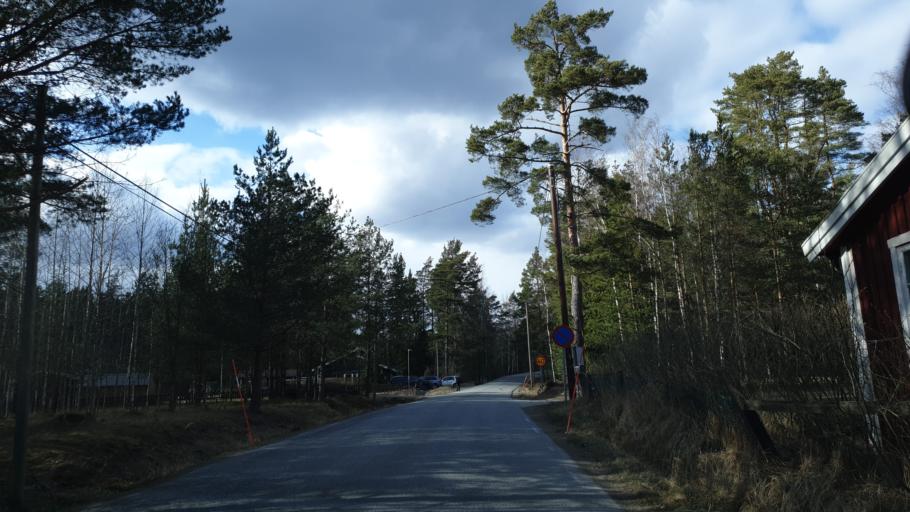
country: SE
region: Stockholm
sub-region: Tyreso Kommun
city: Brevik
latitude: 59.2461
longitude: 18.4416
